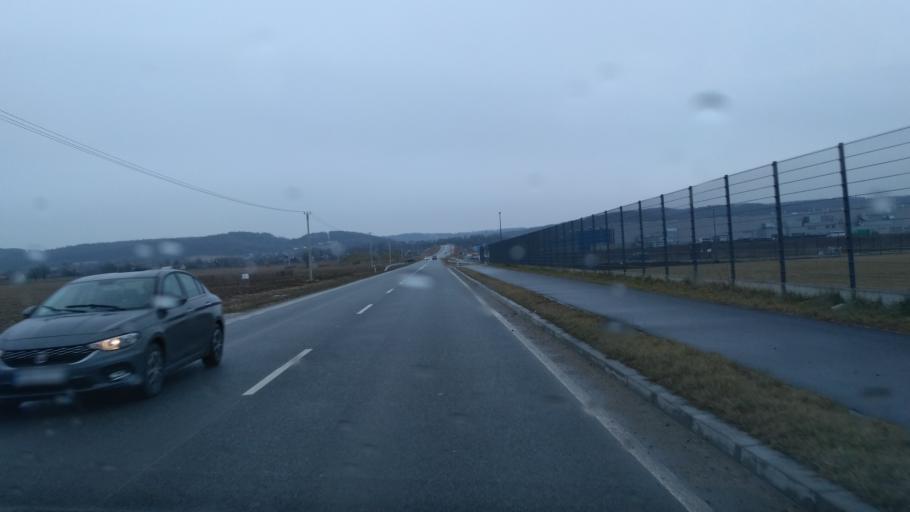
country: PL
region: Subcarpathian Voivodeship
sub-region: Powiat debicki
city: Brzeznica
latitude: 50.0719
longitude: 21.4704
